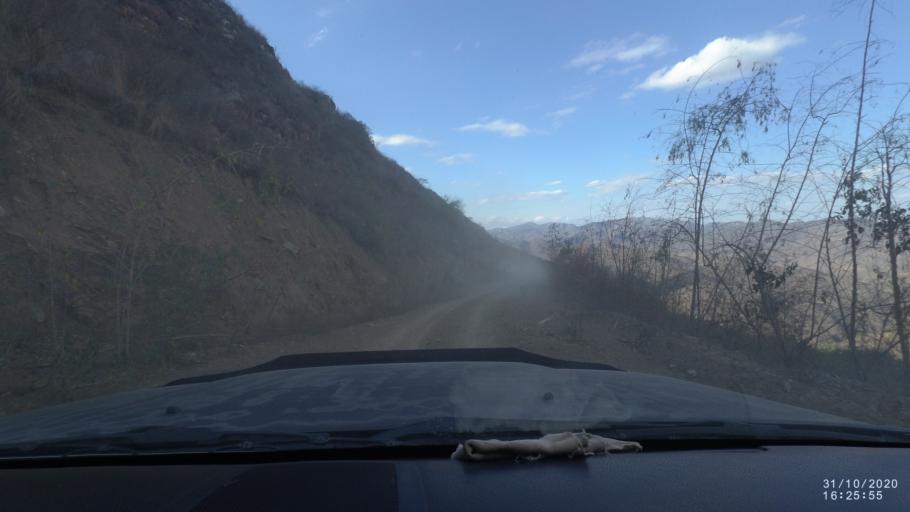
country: BO
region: Chuquisaca
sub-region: Provincia Zudanez
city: Mojocoya
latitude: -18.3976
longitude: -64.5870
